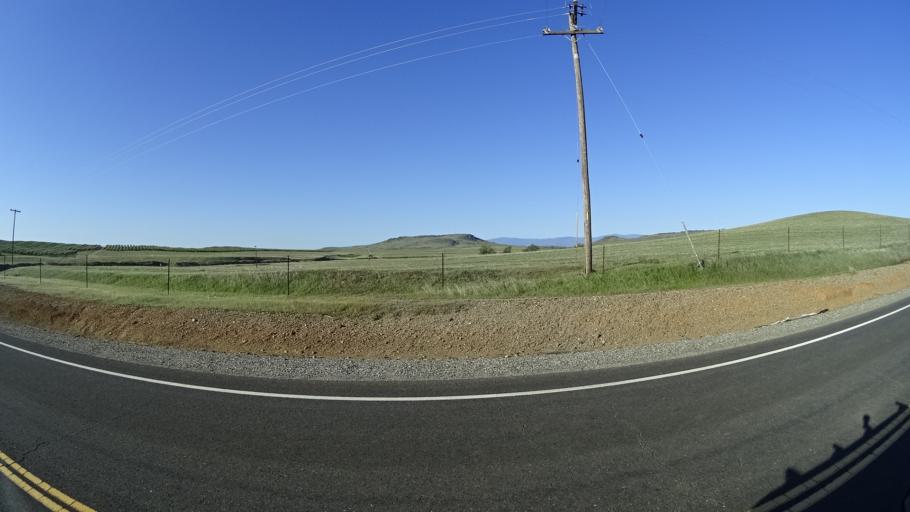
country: US
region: California
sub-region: Glenn County
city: Orland
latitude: 39.7827
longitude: -122.2957
